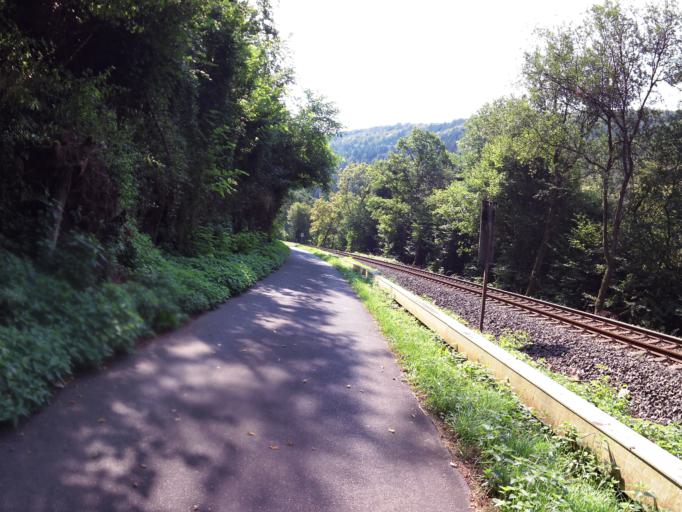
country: DE
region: Rheinland-Pfalz
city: Dahlem
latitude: 49.9137
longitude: 6.6109
